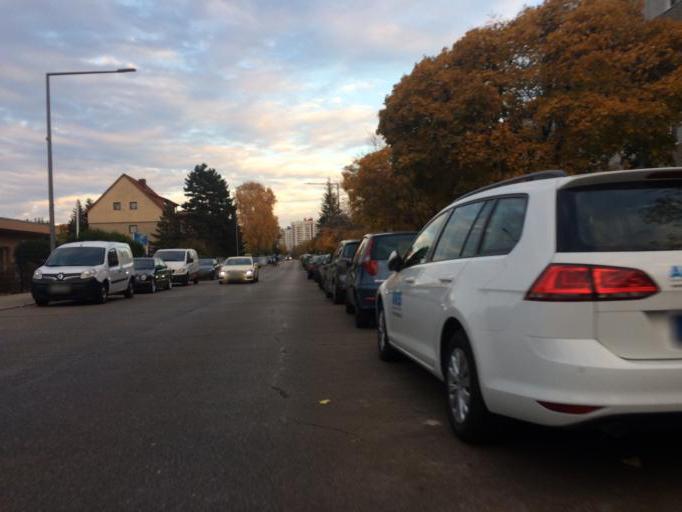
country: DE
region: Berlin
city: Markisches Viertel
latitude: 52.5921
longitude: 13.3501
